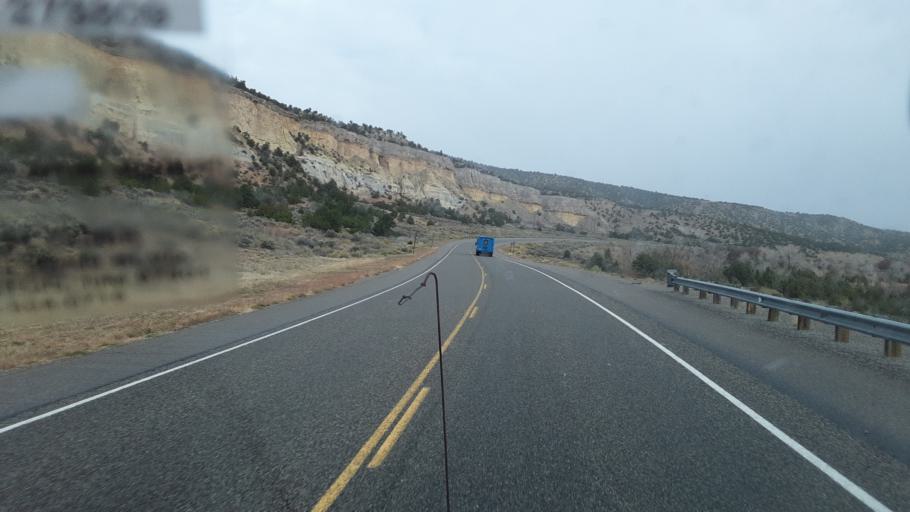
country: US
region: New Mexico
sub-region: Rio Arriba County
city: Santa Teresa
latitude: 36.3778
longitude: -106.5037
